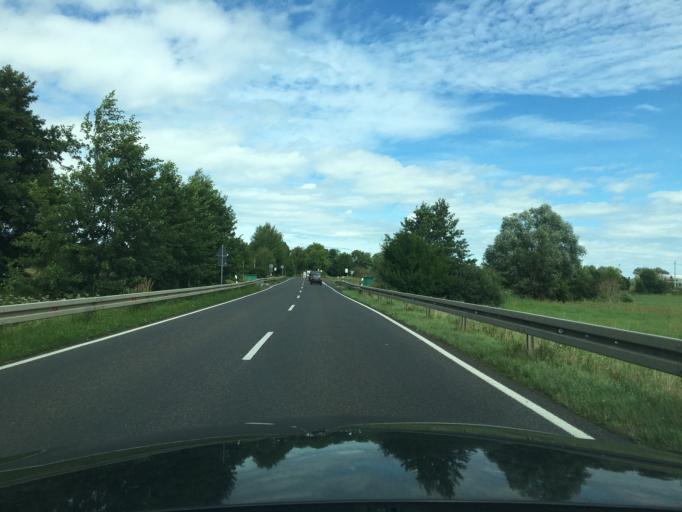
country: DE
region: Brandenburg
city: Gransee
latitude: 53.0182
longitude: 13.1838
